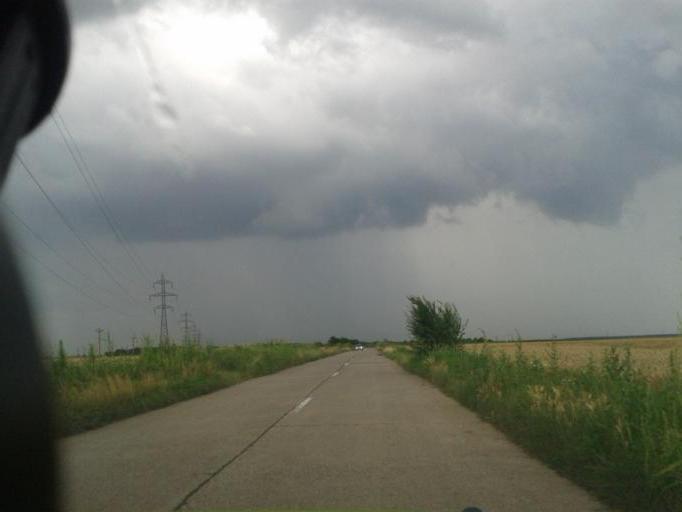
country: RO
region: Calarasi
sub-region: Comuna Belciugatele
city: Belciugatele
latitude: 44.5423
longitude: 26.4542
